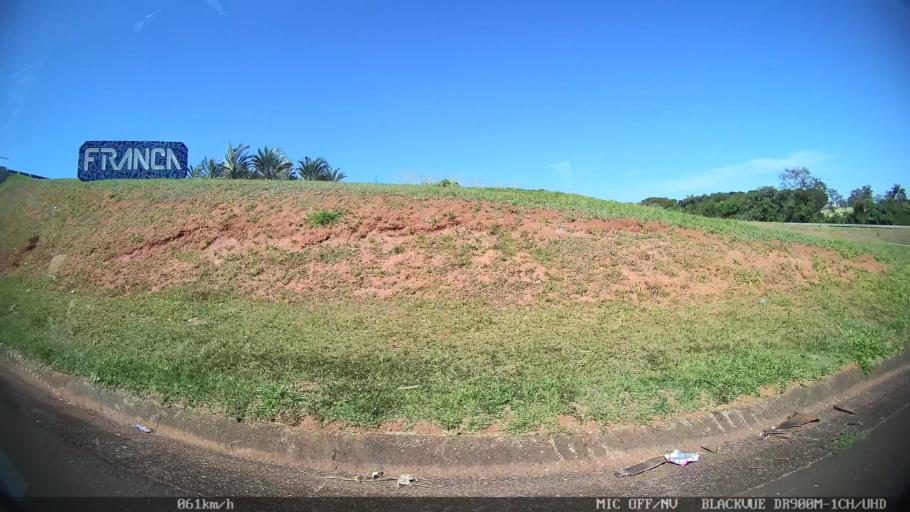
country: BR
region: Sao Paulo
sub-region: Franca
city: Franca
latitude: -20.5621
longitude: -47.4137
